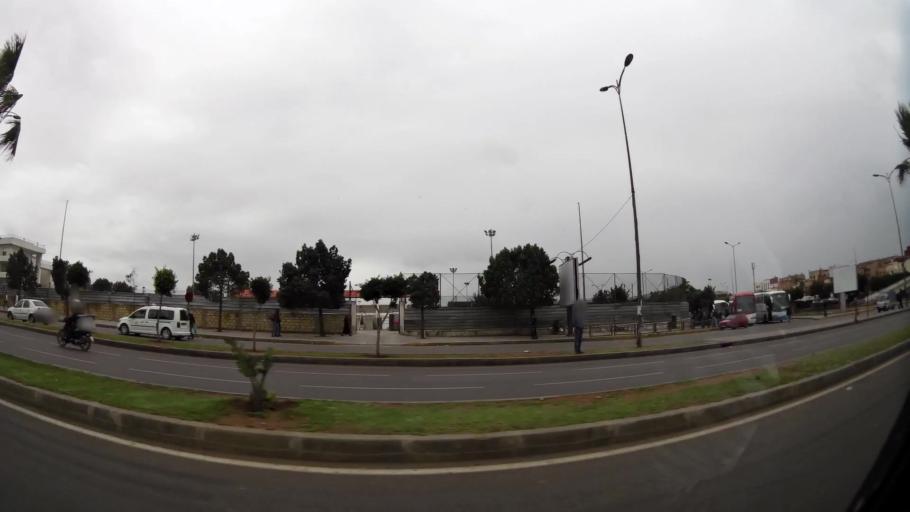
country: MA
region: Grand Casablanca
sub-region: Casablanca
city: Casablanca
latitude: 33.5762
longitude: -7.5858
